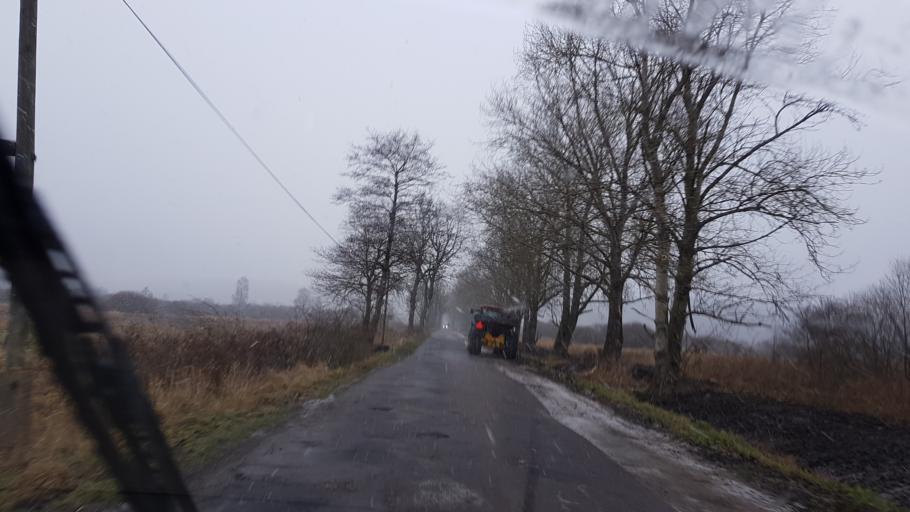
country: PL
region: West Pomeranian Voivodeship
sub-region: Powiat slawienski
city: Slawno
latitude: 54.2614
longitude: 16.5848
